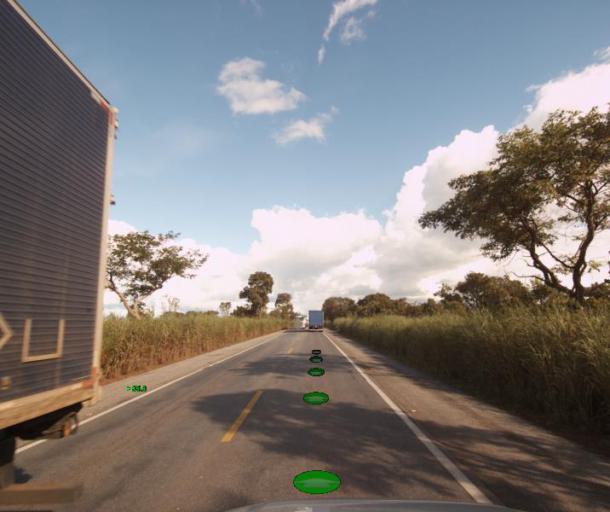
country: BR
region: Goias
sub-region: Porangatu
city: Porangatu
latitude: -13.1372
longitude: -49.1906
